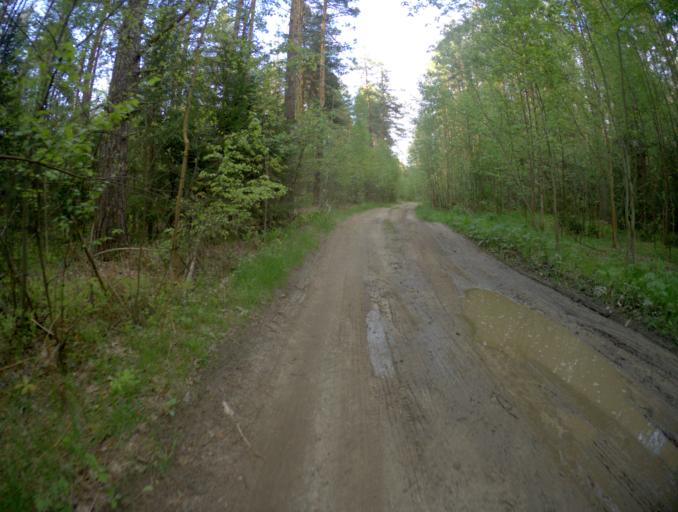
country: RU
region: Rjazan
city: Spas-Klepiki
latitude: 55.2515
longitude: 40.0950
